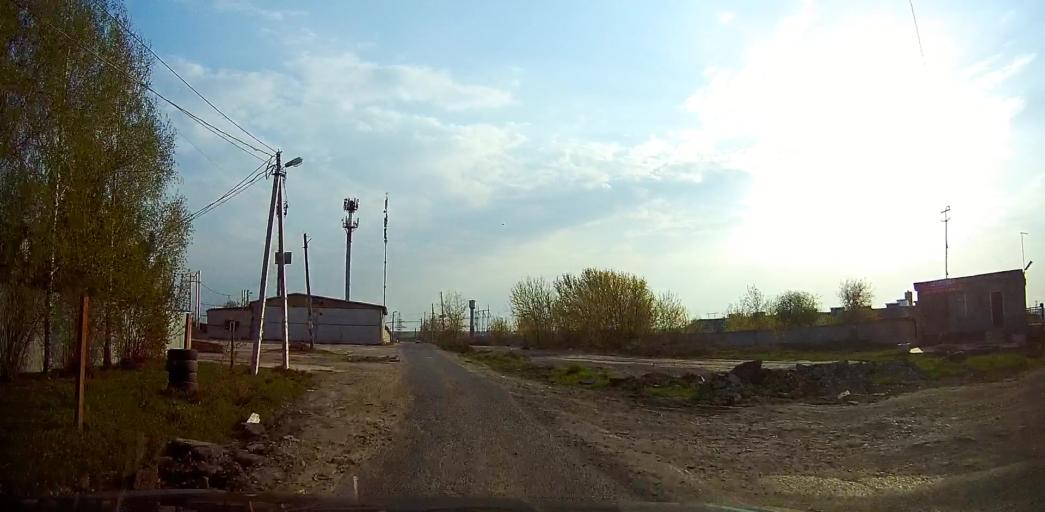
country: RU
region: Moskovskaya
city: Andreyevskoye
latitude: 55.5411
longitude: 37.9731
